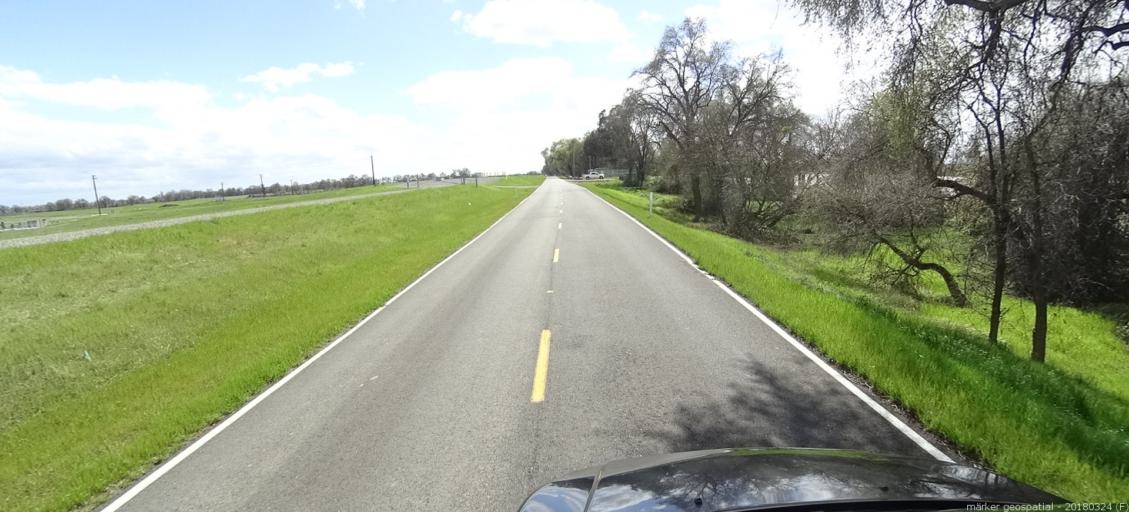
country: US
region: California
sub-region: Sacramento County
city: Elverta
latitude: 38.7321
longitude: -121.6027
